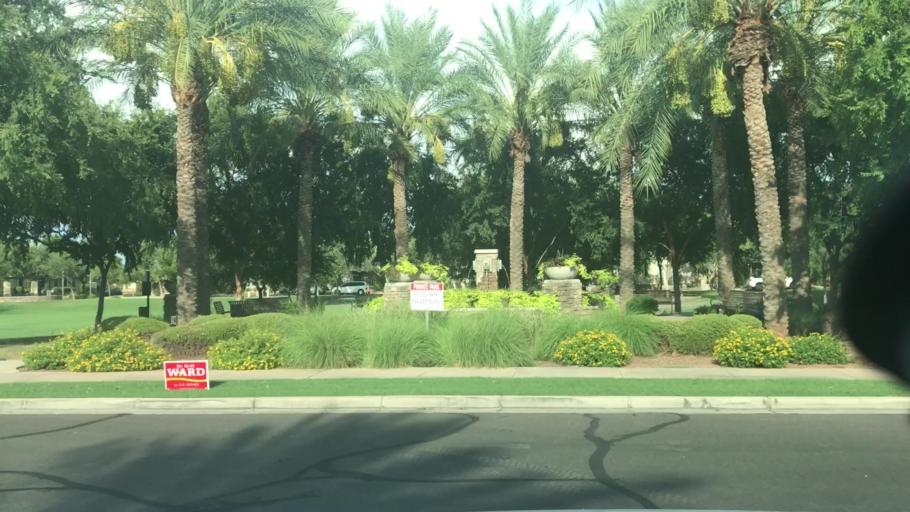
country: US
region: Arizona
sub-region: Maricopa County
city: Gilbert
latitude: 33.3250
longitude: -111.7175
